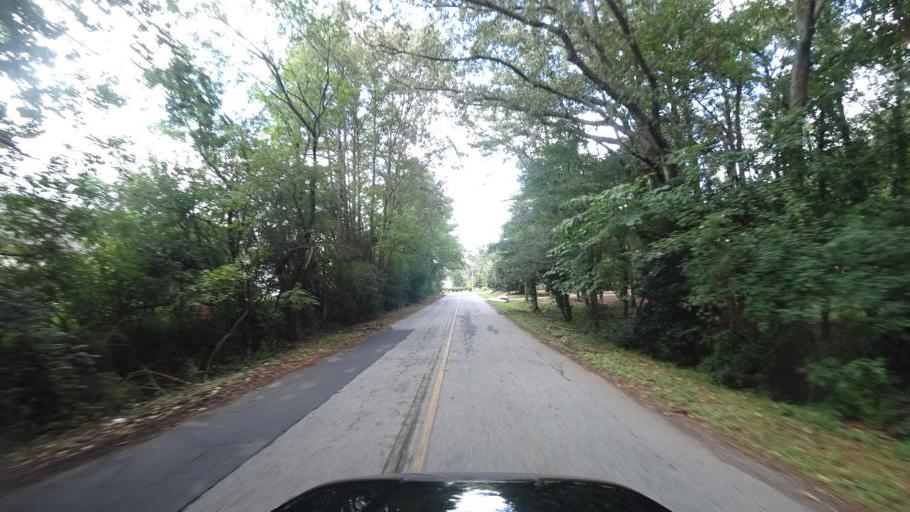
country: US
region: Georgia
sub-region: DeKalb County
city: Panthersville
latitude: 33.6542
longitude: -84.2254
